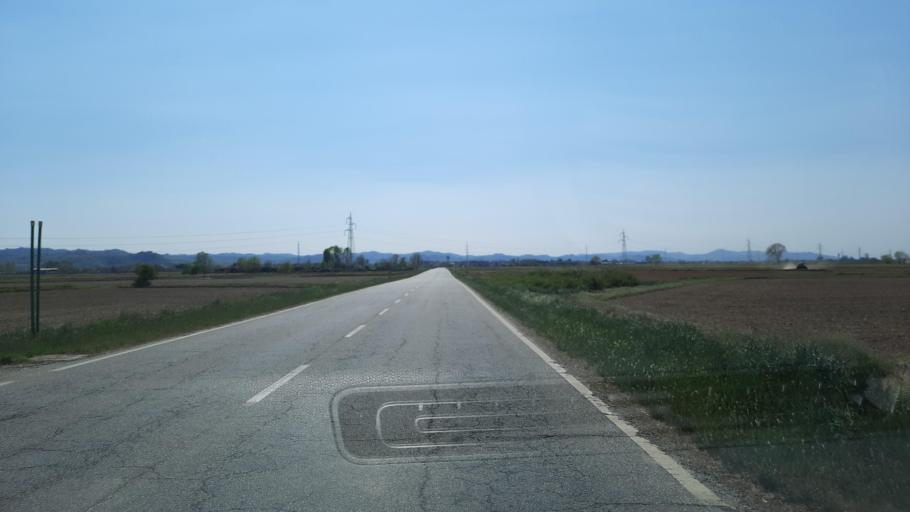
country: IT
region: Piedmont
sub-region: Provincia di Vercelli
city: Lamporo
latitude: 45.2090
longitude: 8.1232
